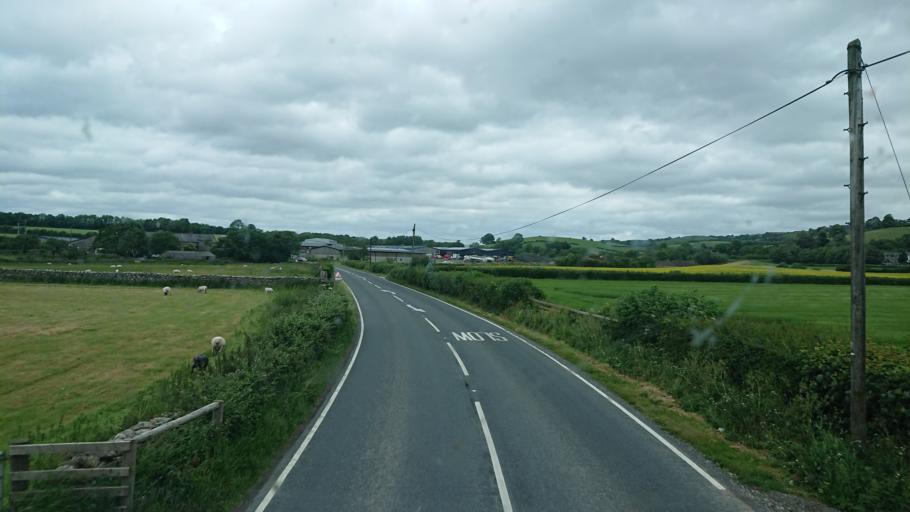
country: GB
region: England
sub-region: Cumbria
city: Milnthorpe
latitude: 54.2298
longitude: -2.7137
